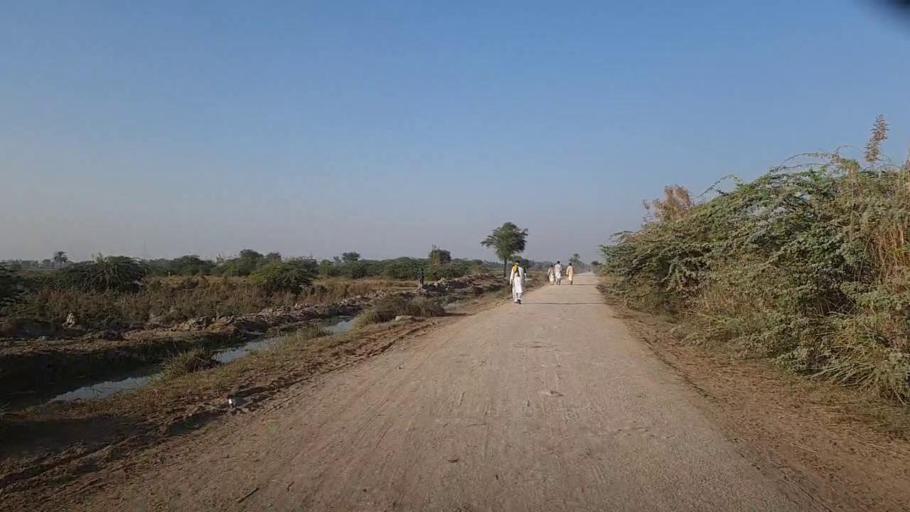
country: PK
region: Sindh
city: Ranipur
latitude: 27.2604
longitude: 68.5121
